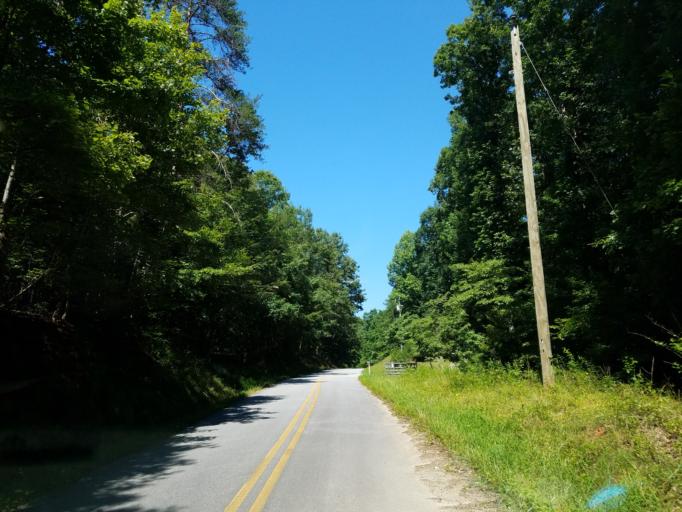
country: US
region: Georgia
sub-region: Lumpkin County
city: Dahlonega
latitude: 34.4189
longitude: -83.9979
